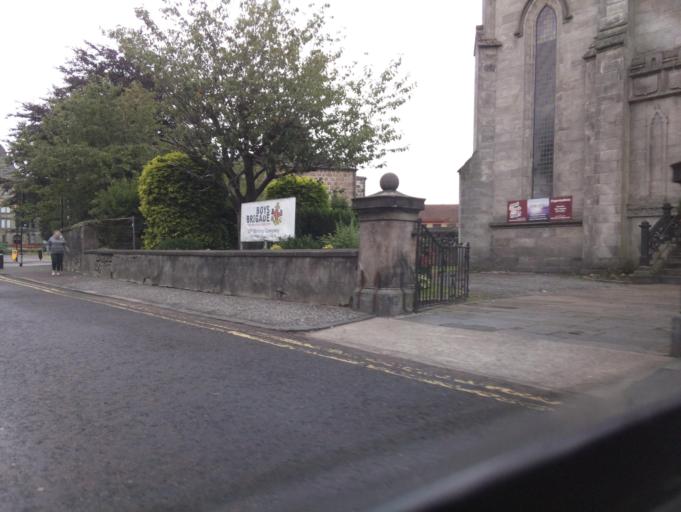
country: GB
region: Scotland
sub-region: Clackmannanshire
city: Alloa
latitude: 56.1162
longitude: -3.7931
